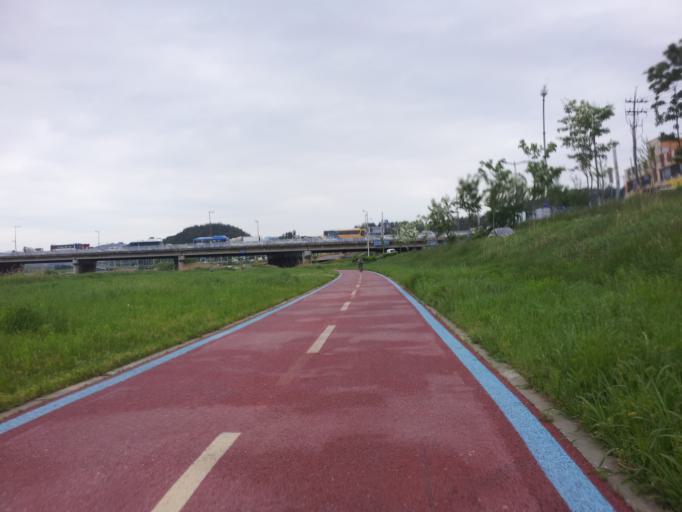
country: KR
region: Daejeon
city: Daejeon
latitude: 36.3553
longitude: 127.4050
